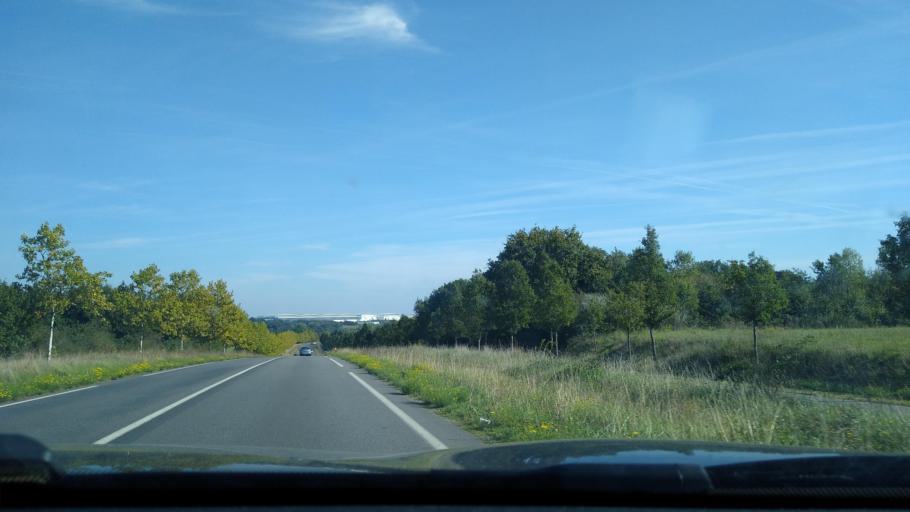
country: FR
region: Midi-Pyrenees
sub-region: Departement de la Haute-Garonne
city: Aussonne
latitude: 43.6654
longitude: 1.3133
